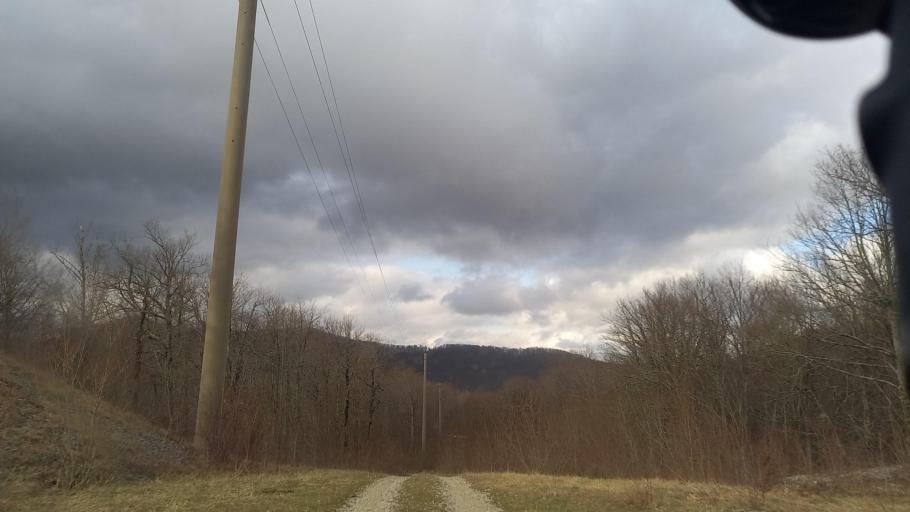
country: RU
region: Krasnodarskiy
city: Dzhubga
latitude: 44.5249
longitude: 38.7729
